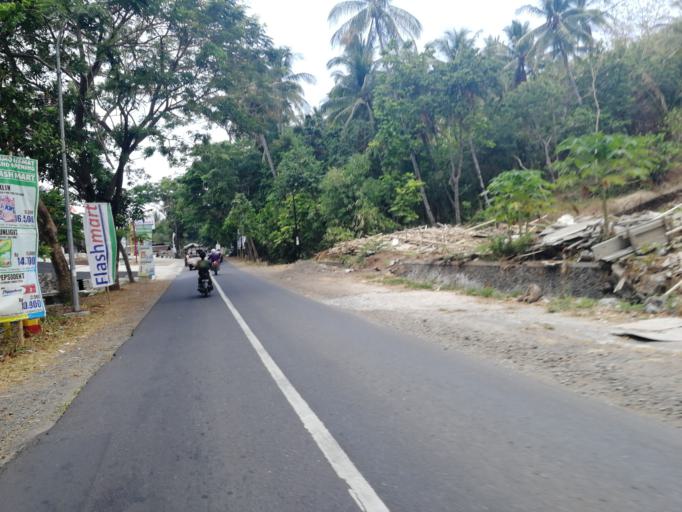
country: ID
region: West Nusa Tenggara
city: Karangsubagan
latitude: -8.4131
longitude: 116.0993
